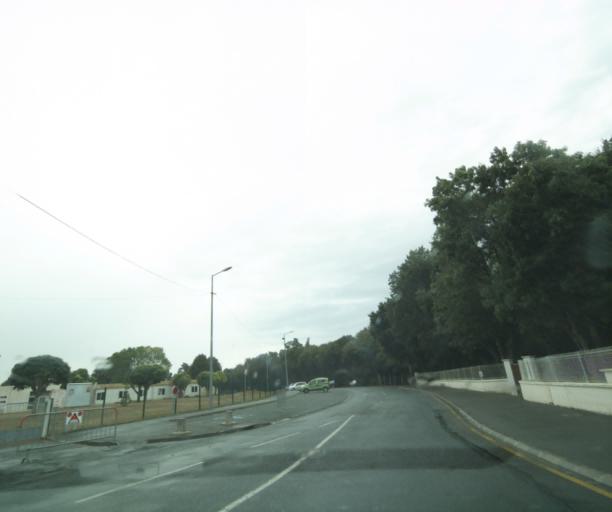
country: FR
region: Poitou-Charentes
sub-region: Departement de la Charente-Maritime
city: Tonnay-Charente
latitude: 45.9456
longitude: -0.9106
